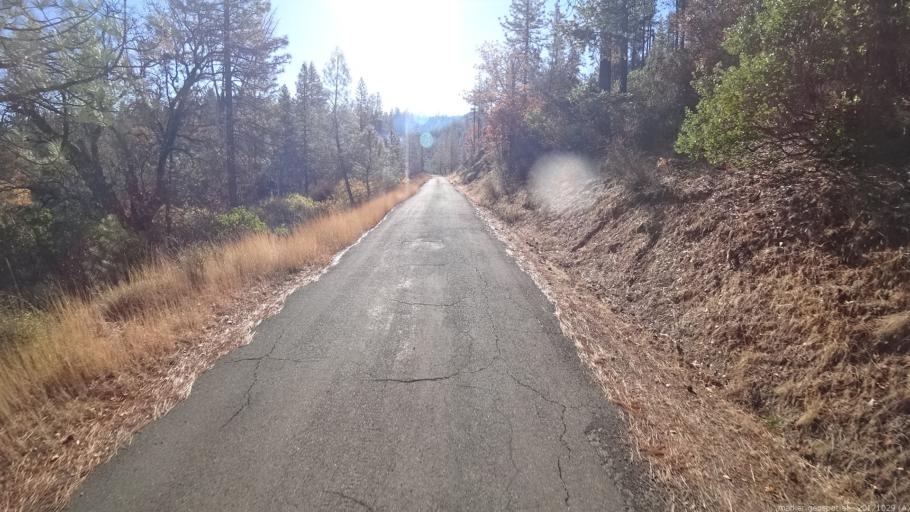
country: US
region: California
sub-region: Trinity County
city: Hayfork
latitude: 40.3613
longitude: -122.9652
